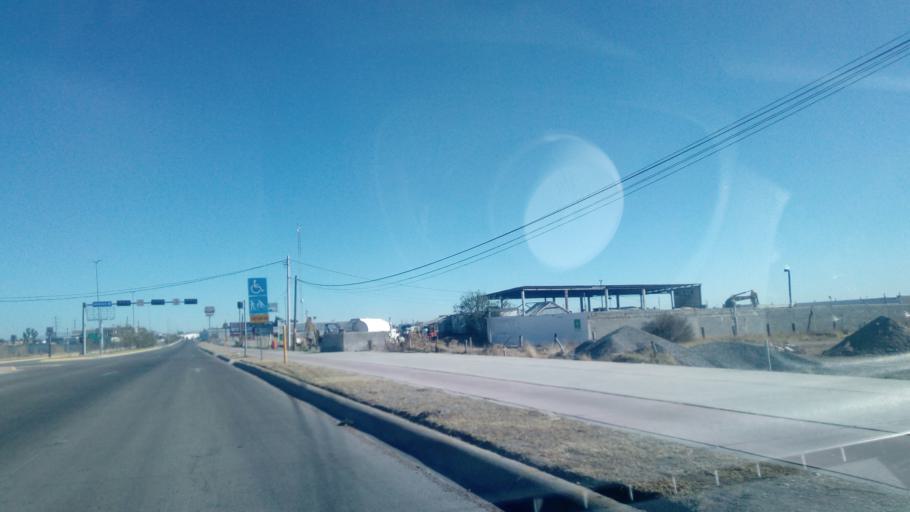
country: MX
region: Durango
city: Victoria de Durango
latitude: 24.0850
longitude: -104.5838
